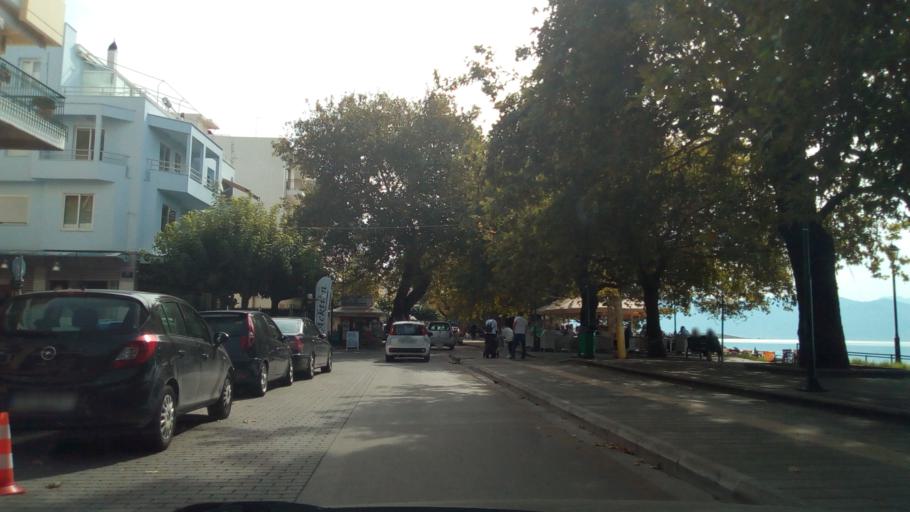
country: GR
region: West Greece
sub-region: Nomos Aitolias kai Akarnanias
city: Nafpaktos
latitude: 38.3920
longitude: 21.8369
